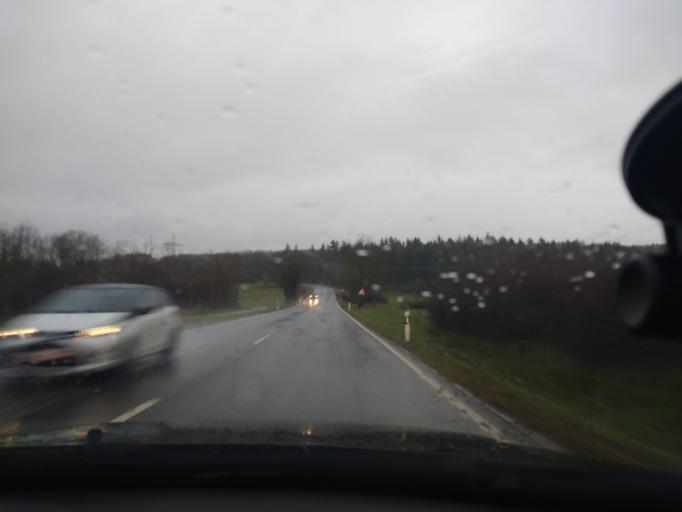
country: DE
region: Rheinland-Pfalz
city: Pellingen
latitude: 49.6961
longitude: 6.6441
